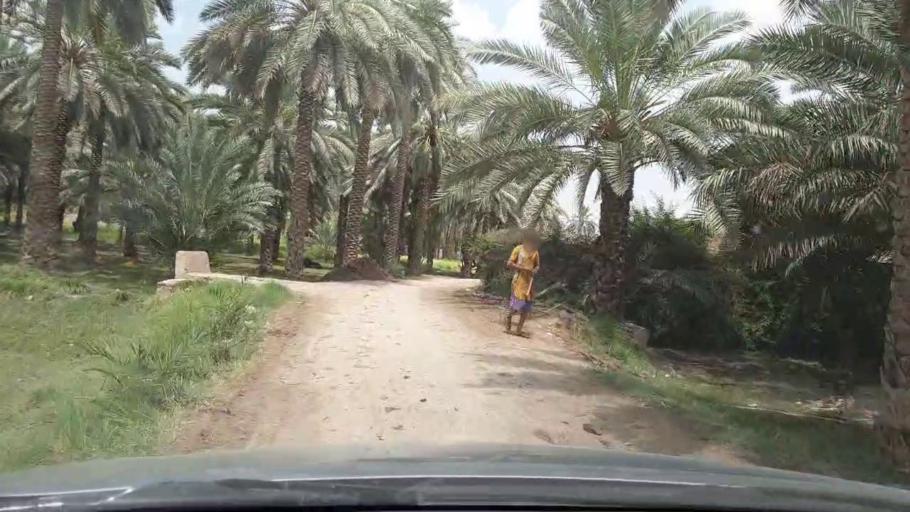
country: PK
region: Sindh
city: Kot Diji
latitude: 27.4230
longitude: 68.7664
